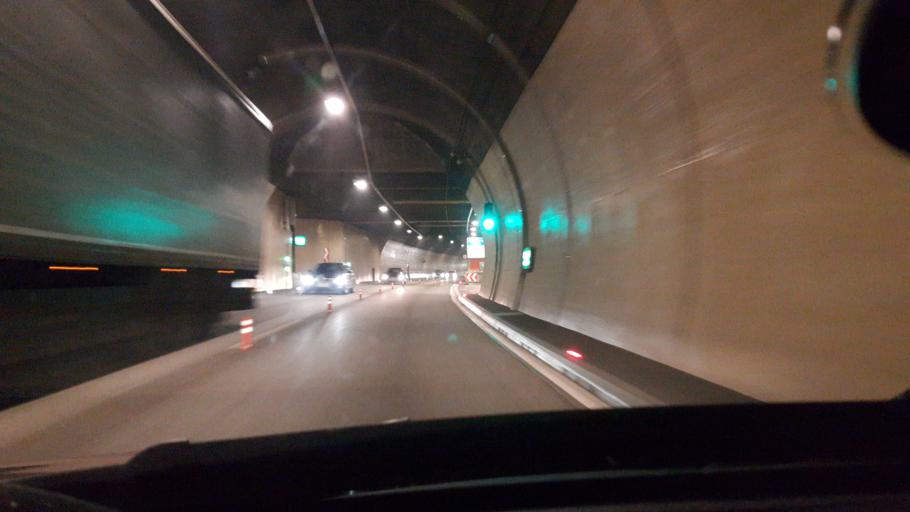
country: AT
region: Carinthia
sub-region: Klagenfurt am Woerthersee
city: Klagenfurt am Woerthersee
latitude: 46.6543
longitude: 14.3084
